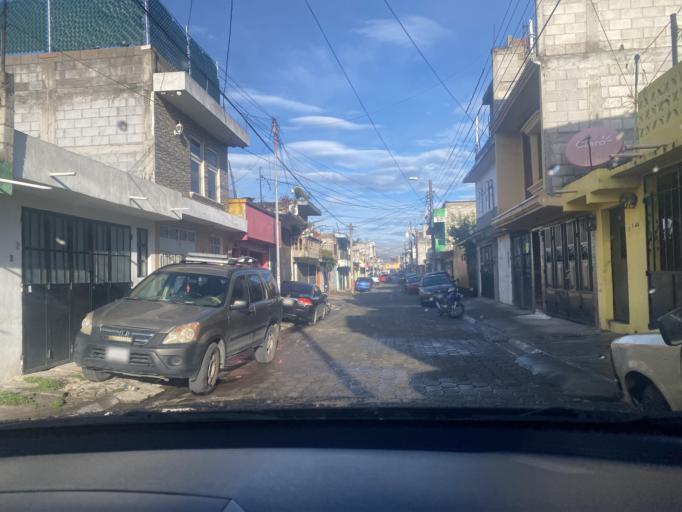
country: GT
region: Quetzaltenango
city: Olintepeque
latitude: 14.8643
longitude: -91.5192
